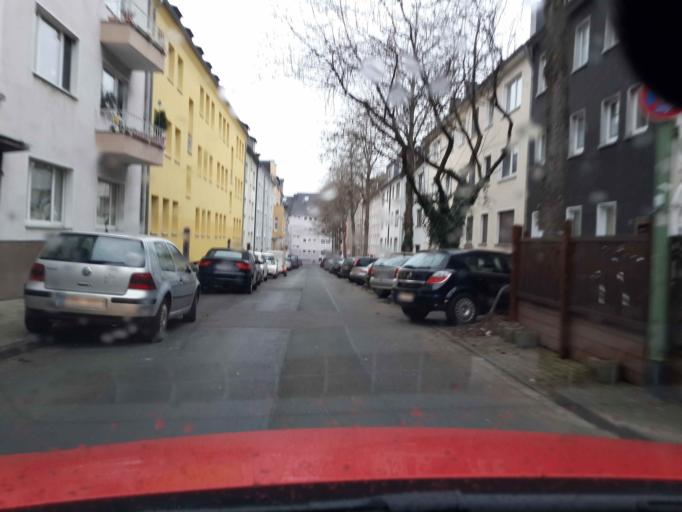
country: DE
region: North Rhine-Westphalia
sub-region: Regierungsbezirk Dusseldorf
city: Essen
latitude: 51.4429
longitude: 7.0169
